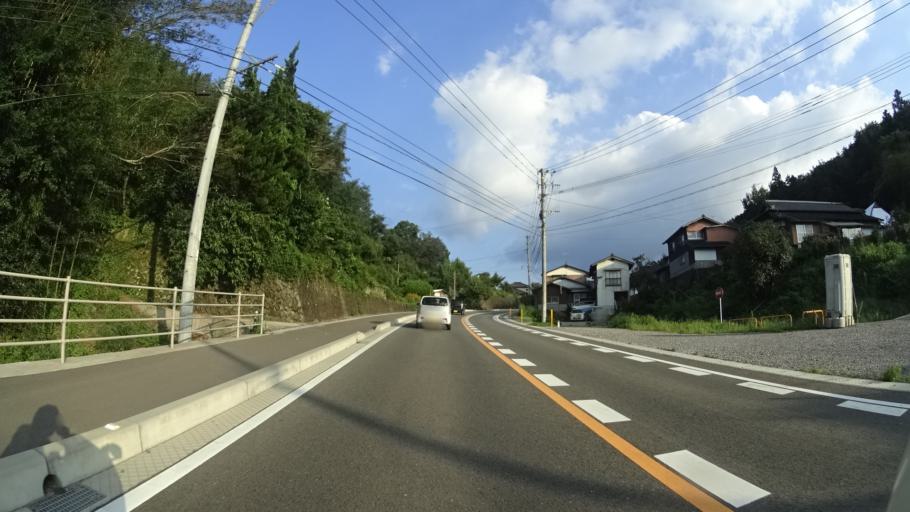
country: JP
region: Oita
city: Hiji
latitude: 33.4118
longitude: 131.3833
